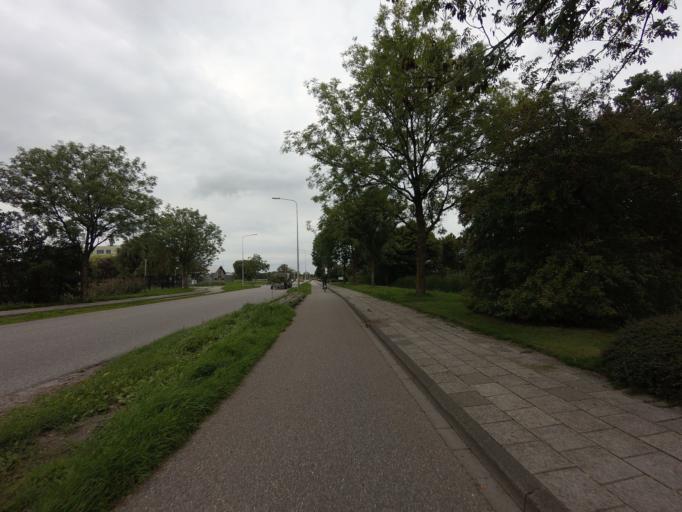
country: NL
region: Friesland
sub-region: Sudwest Fryslan
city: Sneek
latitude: 53.0381
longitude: 5.6451
